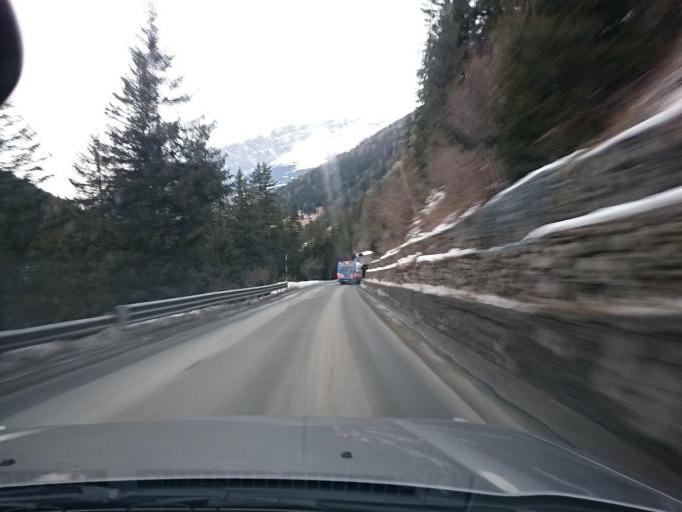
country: IT
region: Lombardy
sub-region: Provincia di Sondrio
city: Sant'Antonio
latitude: 46.4326
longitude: 10.4559
